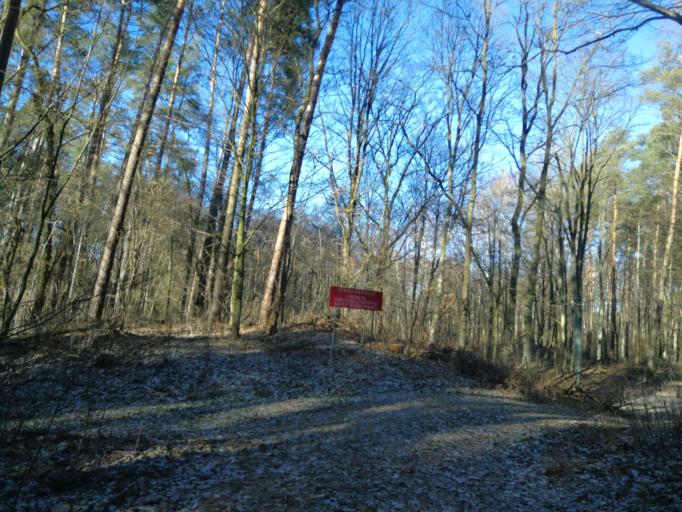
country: PL
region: Kujawsko-Pomorskie
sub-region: Powiat brodnicki
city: Gorzno
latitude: 53.2207
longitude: 19.6649
